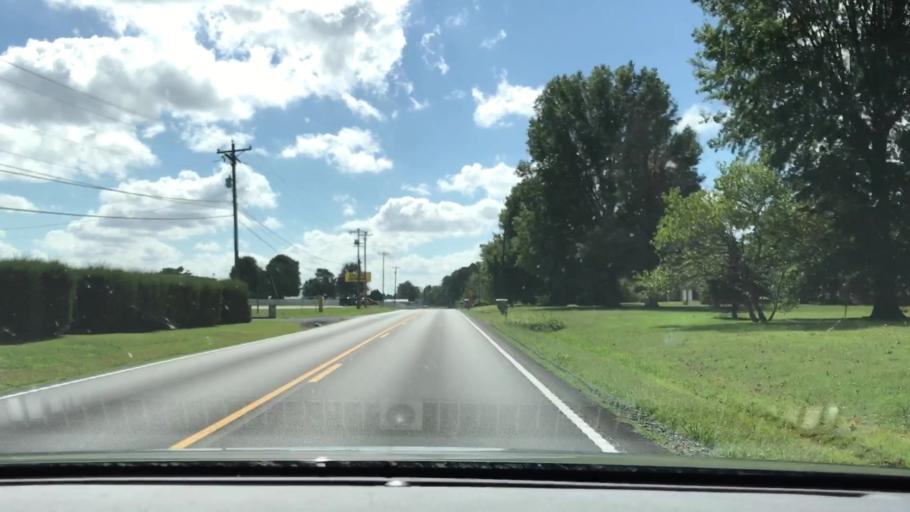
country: US
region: Kentucky
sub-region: Graves County
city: Mayfield
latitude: 36.7644
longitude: -88.5961
